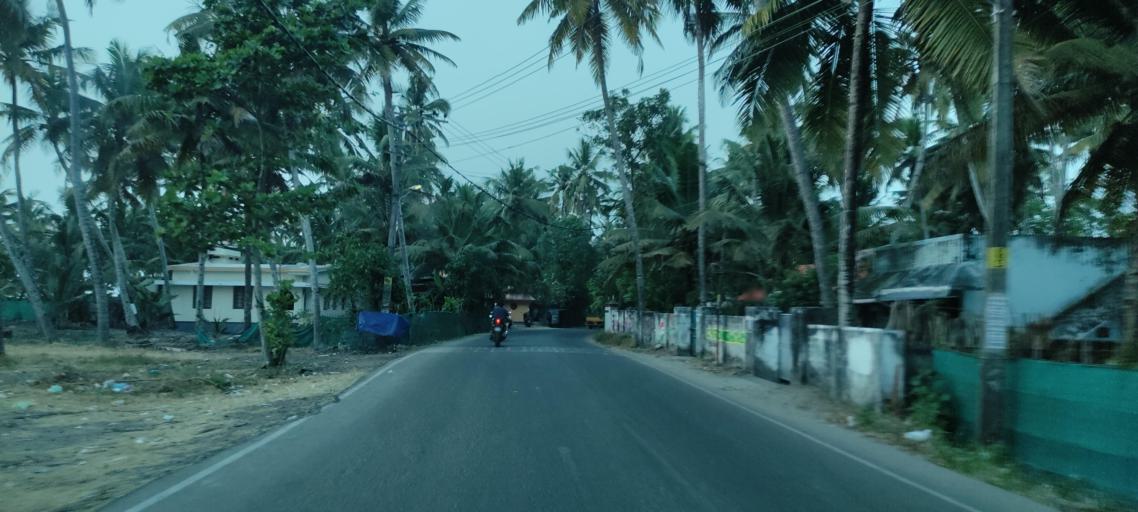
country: IN
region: Kerala
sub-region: Alappuzha
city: Kayankulam
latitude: 9.1142
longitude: 76.4735
